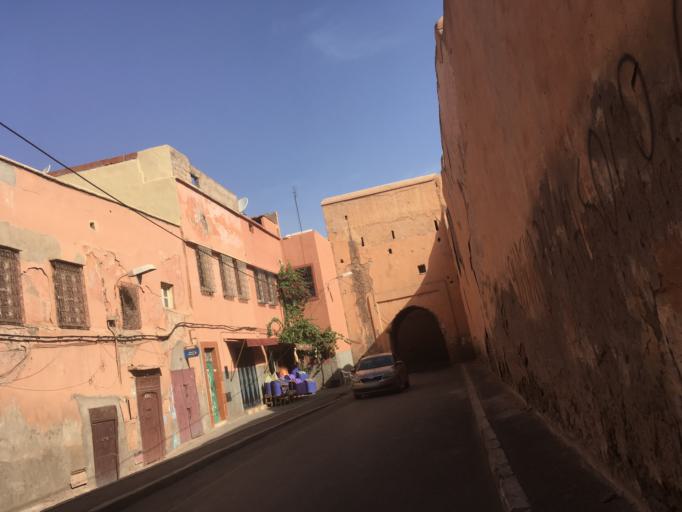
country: MA
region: Marrakech-Tensift-Al Haouz
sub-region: Marrakech
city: Marrakesh
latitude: 31.6208
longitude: -7.9818
